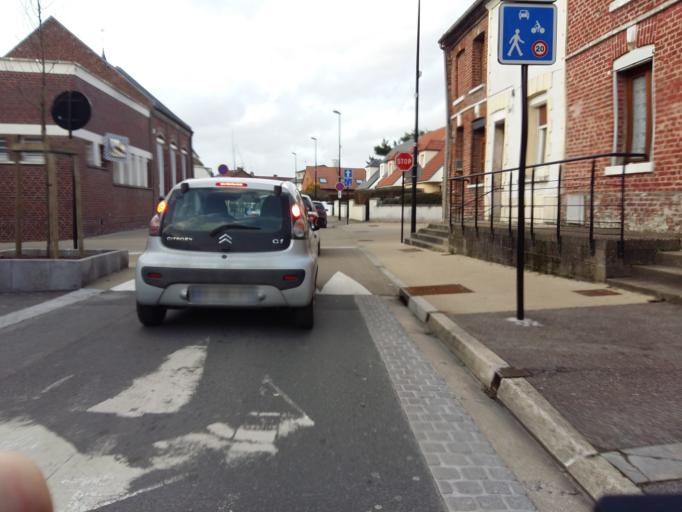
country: FR
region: Picardie
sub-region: Departement de la Somme
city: Camon
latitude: 49.8863
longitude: 2.3471
